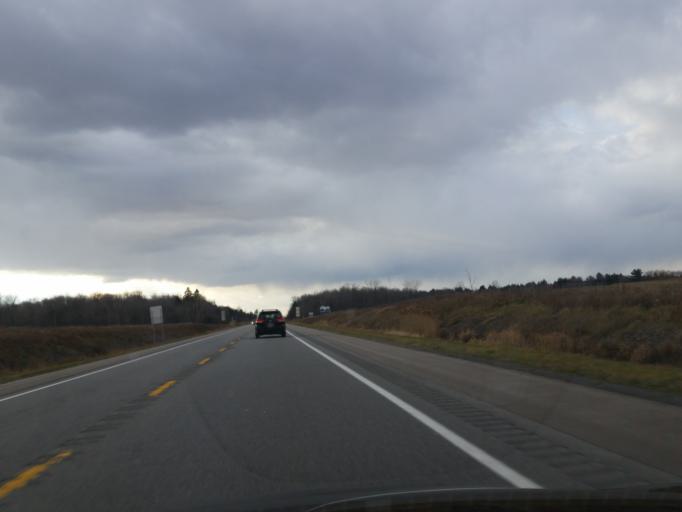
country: CA
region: Quebec
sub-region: Laurentides
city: Lachute
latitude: 45.6455
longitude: -74.2490
